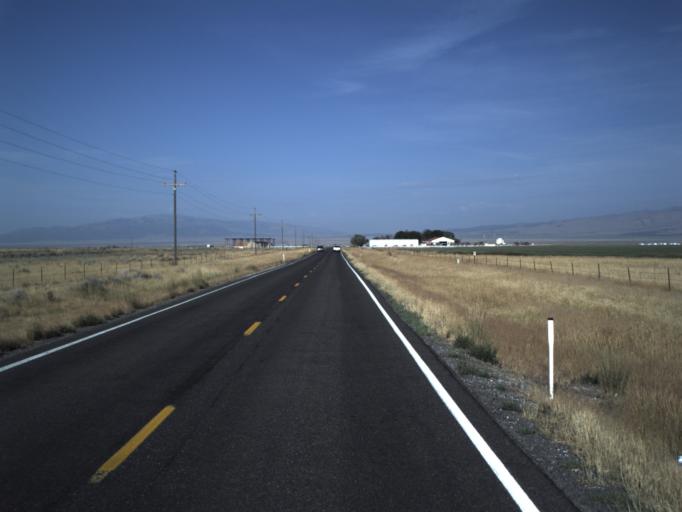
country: US
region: Idaho
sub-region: Oneida County
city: Malad City
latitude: 41.9671
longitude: -112.7963
